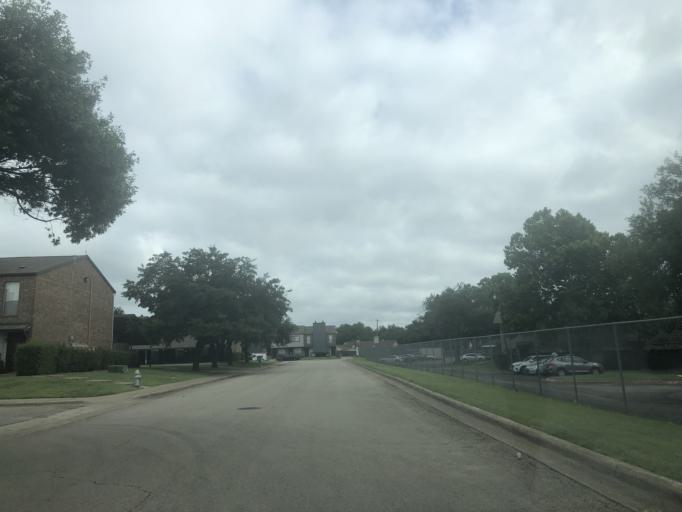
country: US
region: Texas
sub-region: Dallas County
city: Duncanville
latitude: 32.6525
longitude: -96.9241
